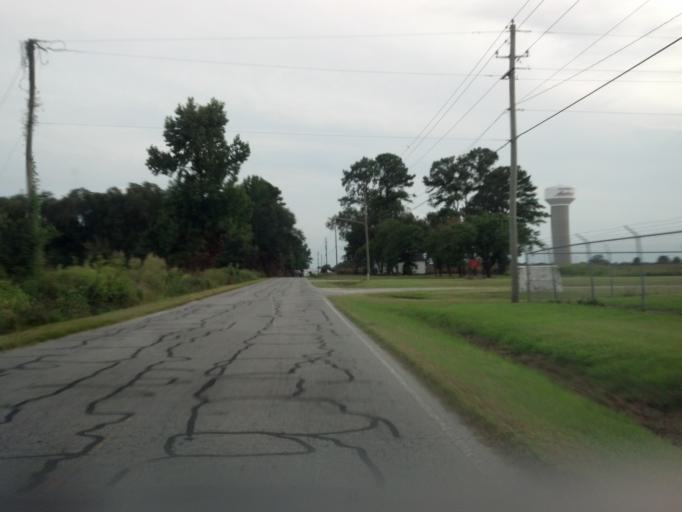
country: US
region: North Carolina
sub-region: Pitt County
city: Ayden
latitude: 35.4878
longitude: -77.4277
